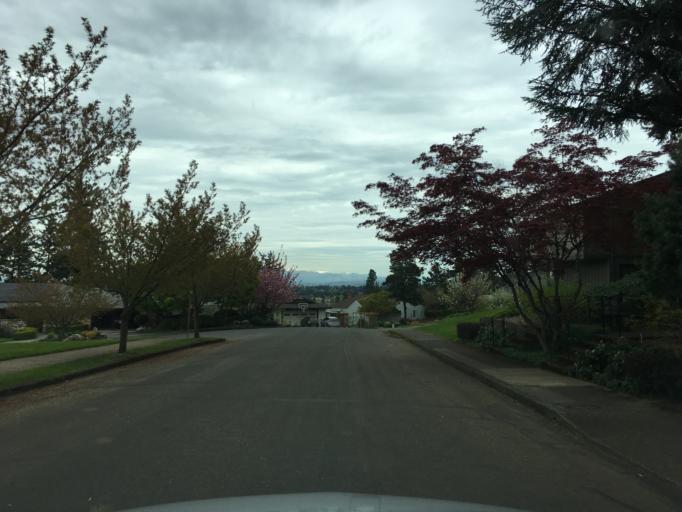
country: US
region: Oregon
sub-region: Multnomah County
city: Lents
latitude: 45.5212
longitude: -122.5939
